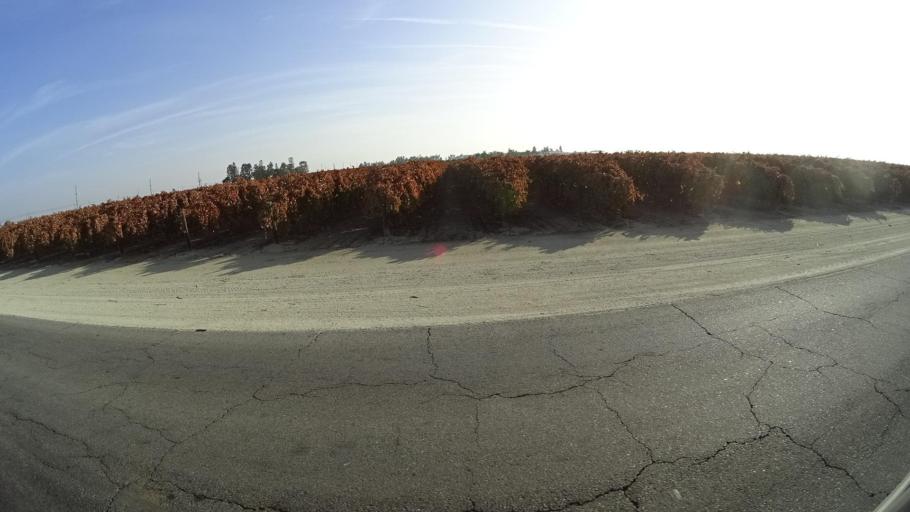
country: US
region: California
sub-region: Kern County
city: Delano
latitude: 35.7740
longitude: -119.1875
